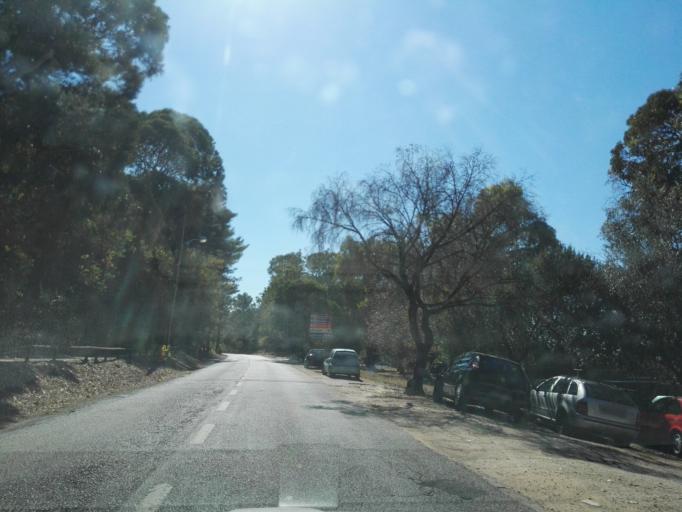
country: PT
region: Lisbon
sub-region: Amadora
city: Amadora
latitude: 38.7330
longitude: -9.2030
